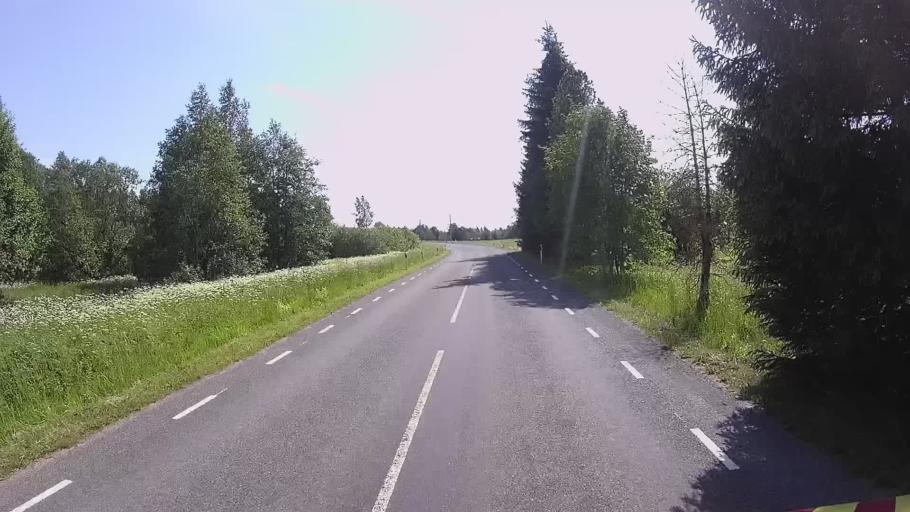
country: EE
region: Viljandimaa
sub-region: Karksi vald
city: Karksi-Nuia
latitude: 58.0509
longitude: 25.5453
